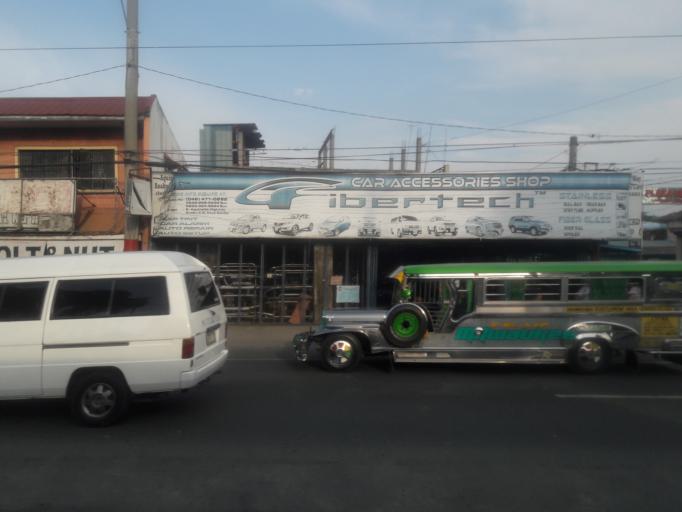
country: PH
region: Calabarzon
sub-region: Province of Cavite
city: Imus
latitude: 14.3848
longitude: 120.9394
